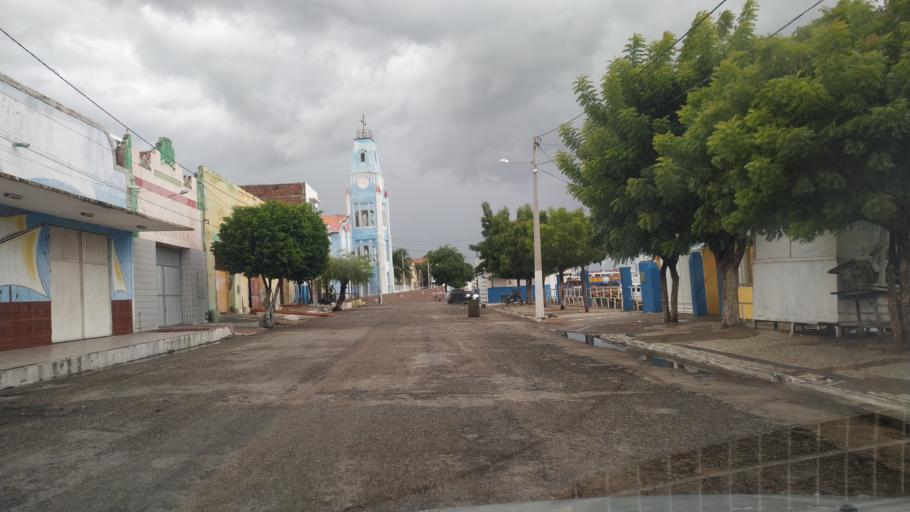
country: BR
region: Rio Grande do Norte
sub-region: Areia Branca
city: Areia Branca
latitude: -4.9552
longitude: -37.1365
